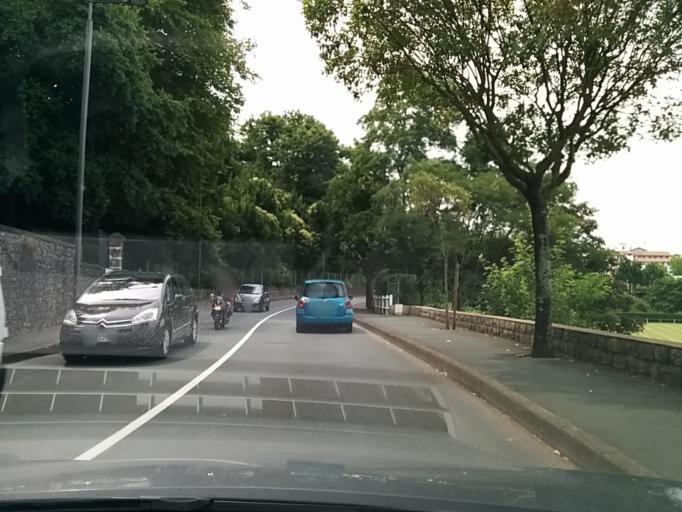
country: FR
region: Aquitaine
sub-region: Departement des Pyrenees-Atlantiques
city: Hendaye
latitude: 43.3633
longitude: -1.7716
